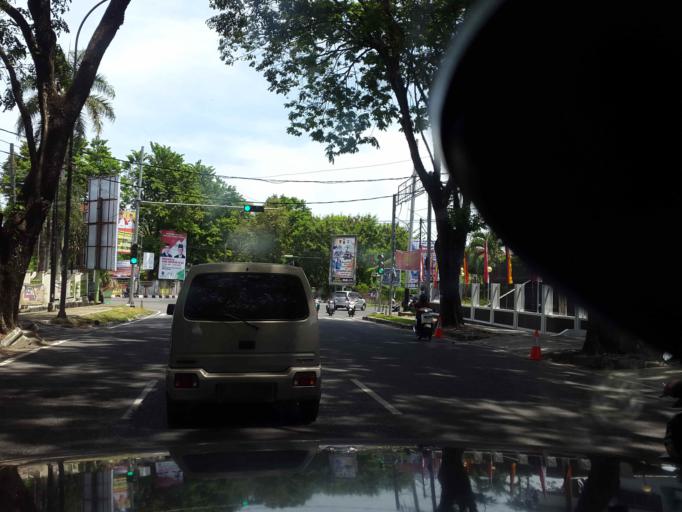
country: ID
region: West Sumatra
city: Padang
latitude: -0.9342
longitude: 100.3621
